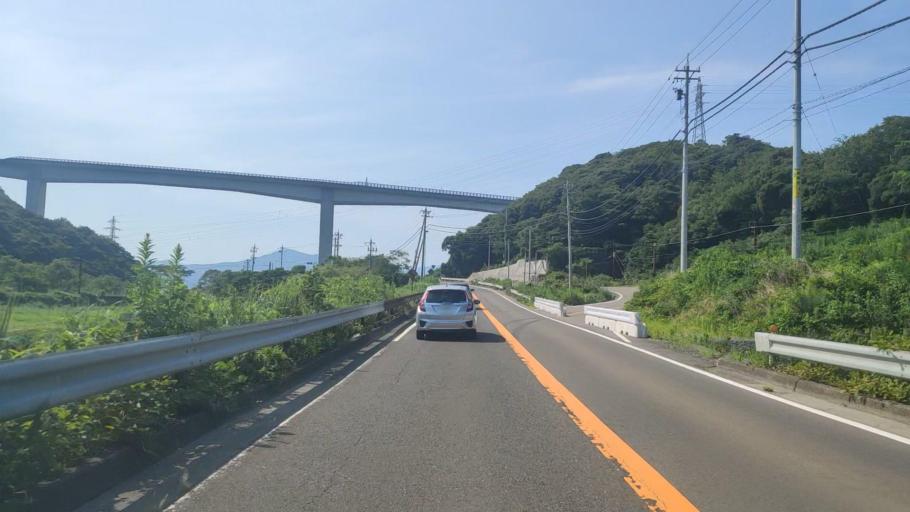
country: JP
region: Fukui
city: Tsuruga
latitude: 35.6210
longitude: 136.0817
